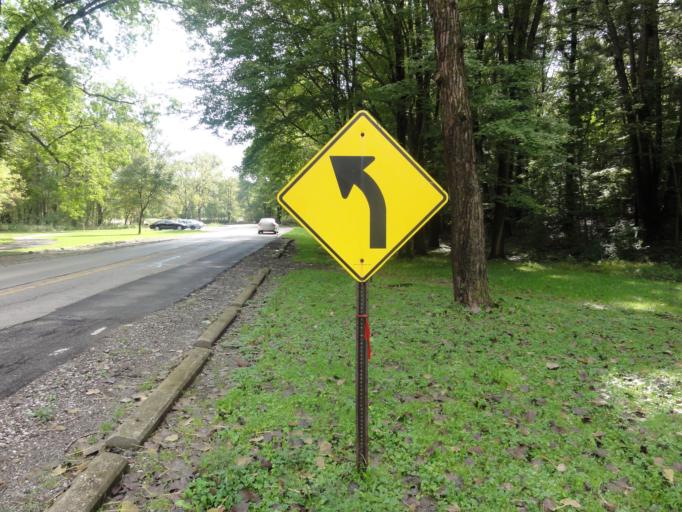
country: US
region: Ohio
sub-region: Cuyahoga County
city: Berea
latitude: 41.3516
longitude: -81.8477
